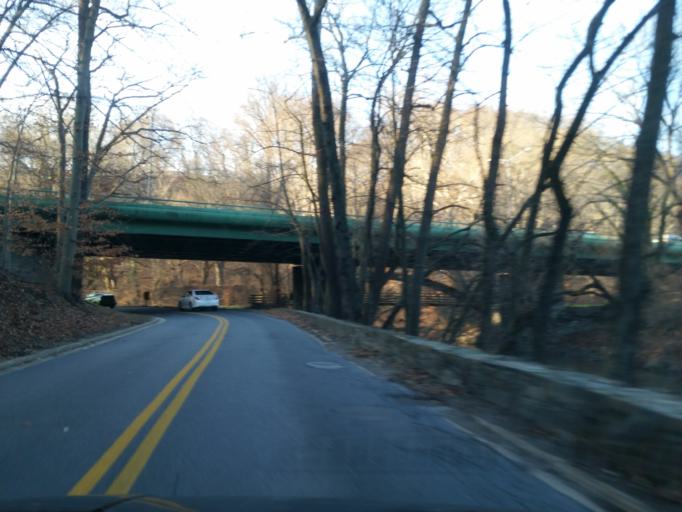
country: US
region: Washington, D.C.
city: Washington, D.C.
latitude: 38.9335
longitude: -77.0496
